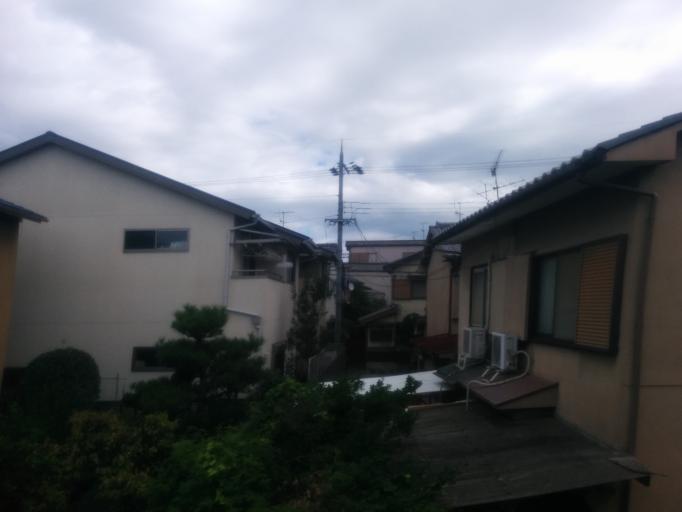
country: JP
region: Kyoto
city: Kyoto
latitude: 34.9573
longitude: 135.7773
